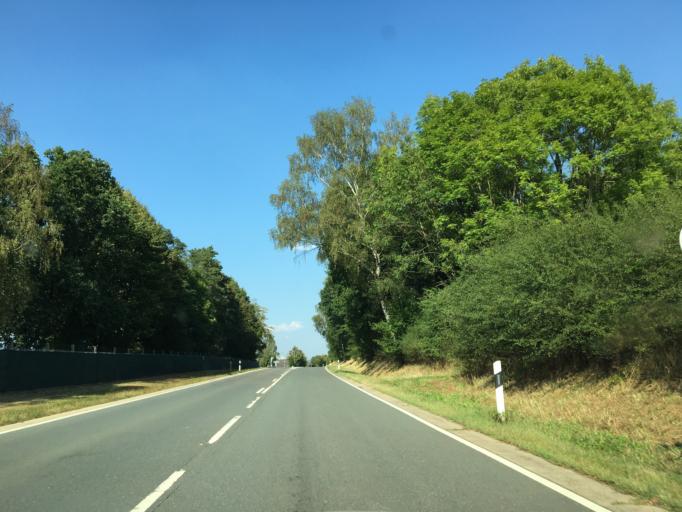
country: DE
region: Hesse
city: Frankenberg
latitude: 51.0362
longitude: 8.7856
